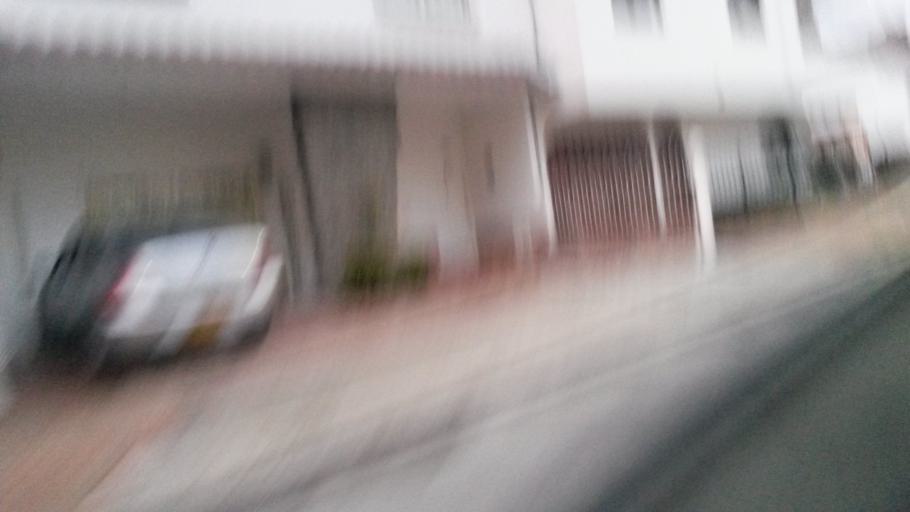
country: CO
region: Quindio
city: Armenia
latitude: 4.5506
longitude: -75.6614
